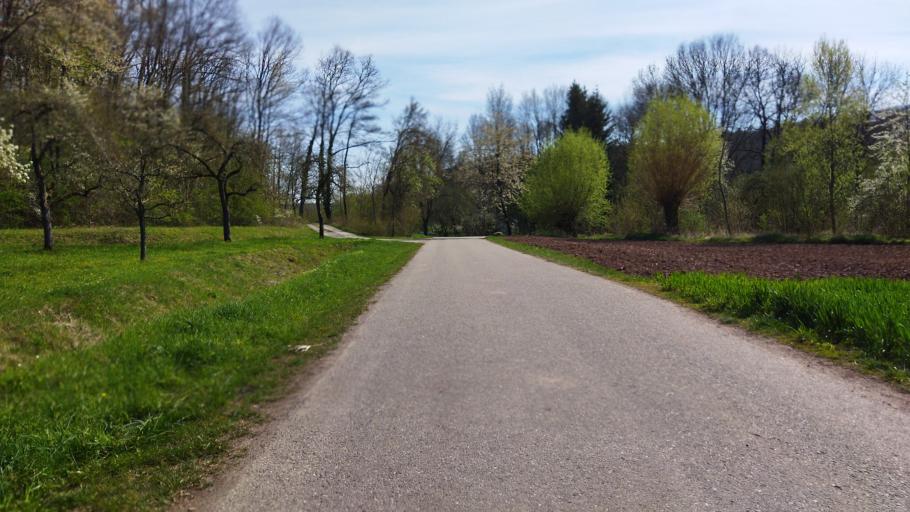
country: DE
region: Baden-Wuerttemberg
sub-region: Regierungsbezirk Stuttgart
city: Sersheim
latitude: 49.0047
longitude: 9.0116
